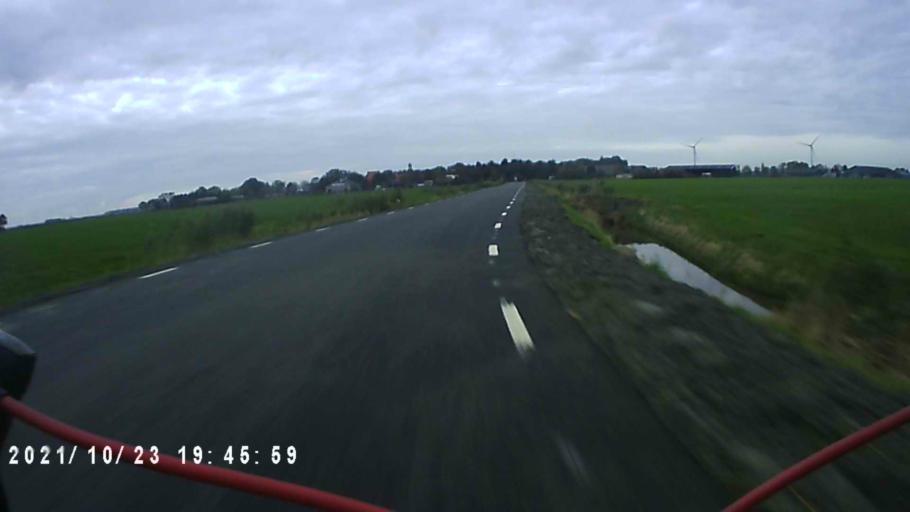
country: NL
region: Friesland
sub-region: Sudwest Fryslan
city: Makkum
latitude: 53.0800
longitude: 5.4269
